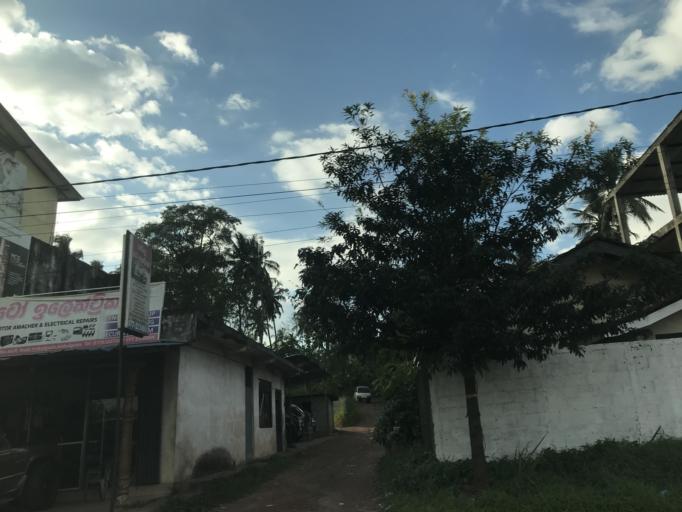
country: LK
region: Western
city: Gampaha
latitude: 7.0506
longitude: 80.0027
